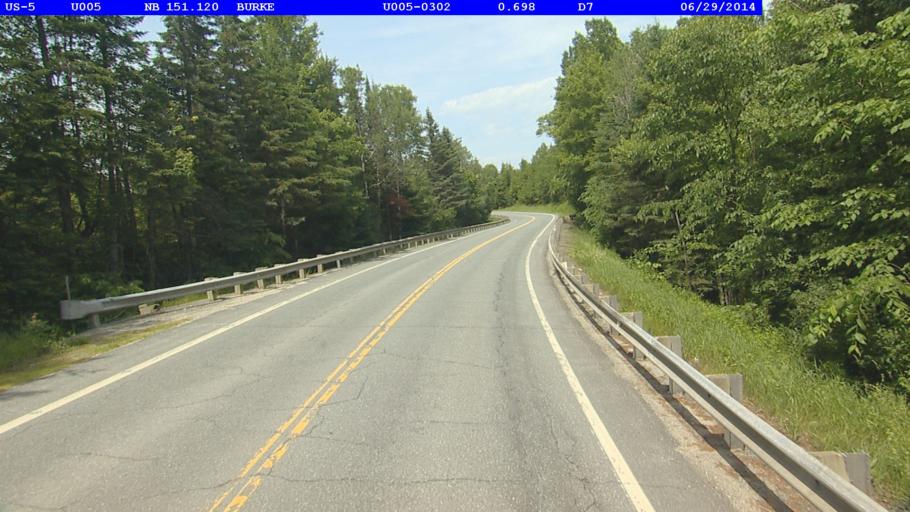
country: US
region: Vermont
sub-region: Caledonia County
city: Lyndonville
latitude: 44.5956
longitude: -71.9751
